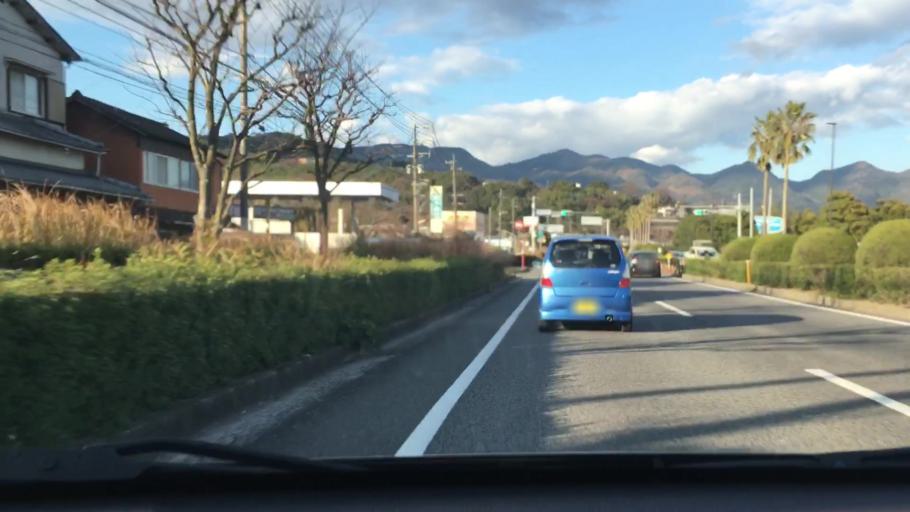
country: JP
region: Oita
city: Hiji
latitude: 33.3413
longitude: 131.4944
